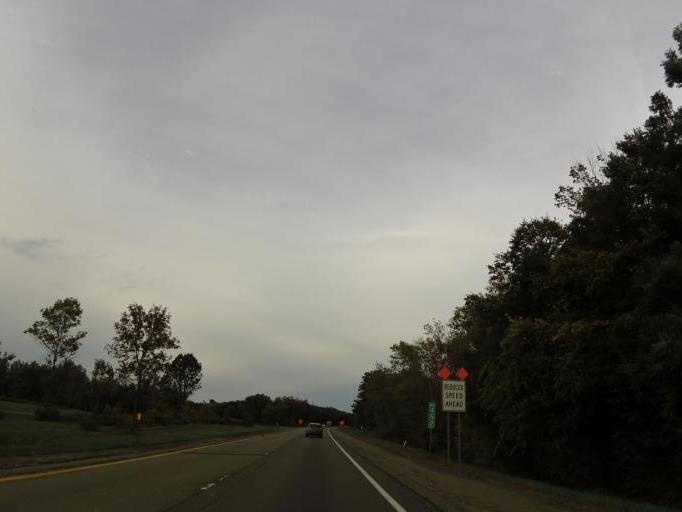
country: US
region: New York
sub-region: Erie County
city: Lake Erie Beach
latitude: 42.5866
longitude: -79.0577
